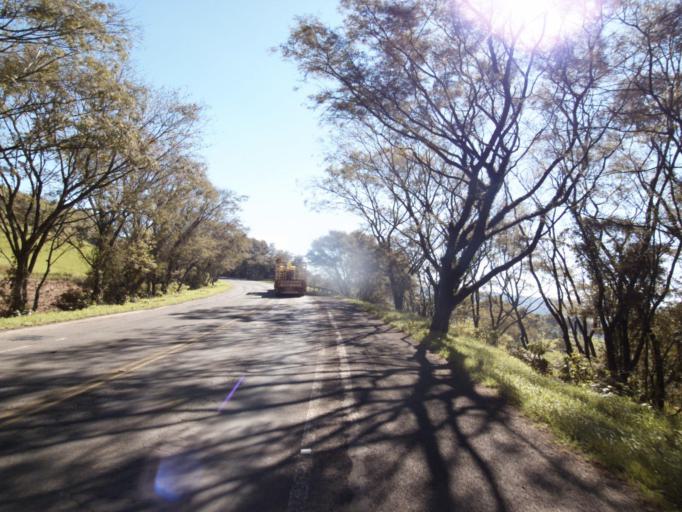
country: BR
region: Rio Grande do Sul
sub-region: Frederico Westphalen
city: Frederico Westphalen
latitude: -26.7940
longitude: -53.4501
